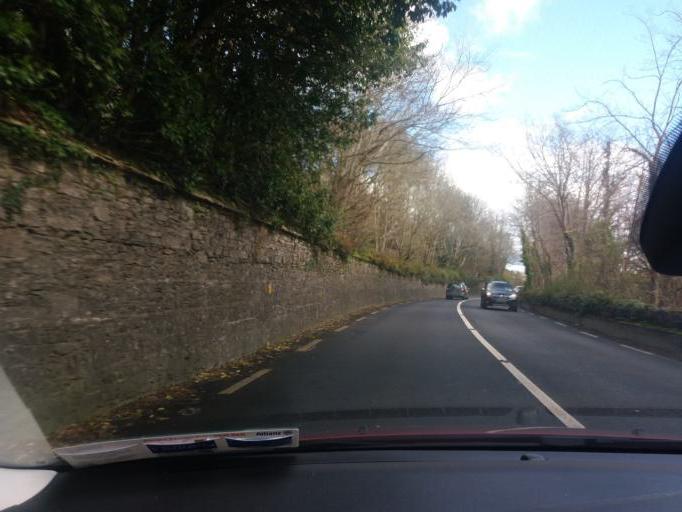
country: IE
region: Munster
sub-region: County Cork
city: Carrigtwohill
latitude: 51.8957
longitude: -8.2817
